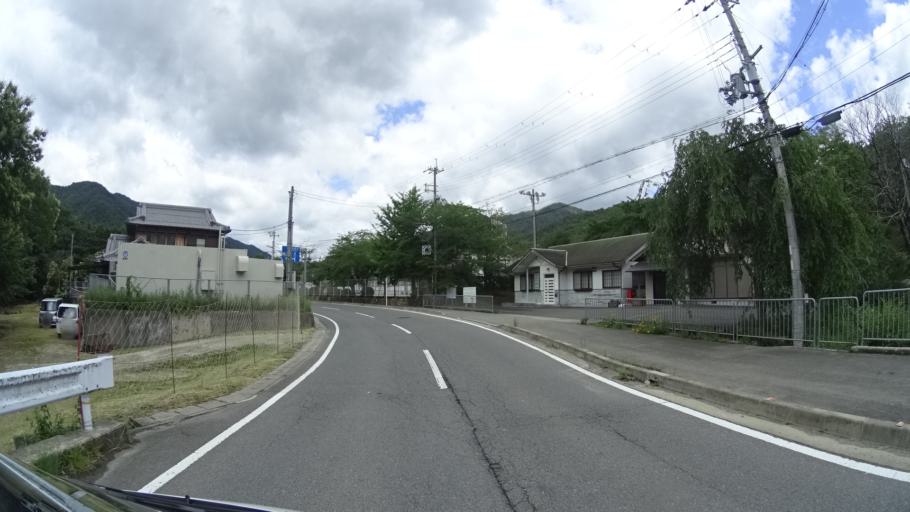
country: JP
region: Kyoto
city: Kameoka
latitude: 35.0142
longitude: 135.4318
